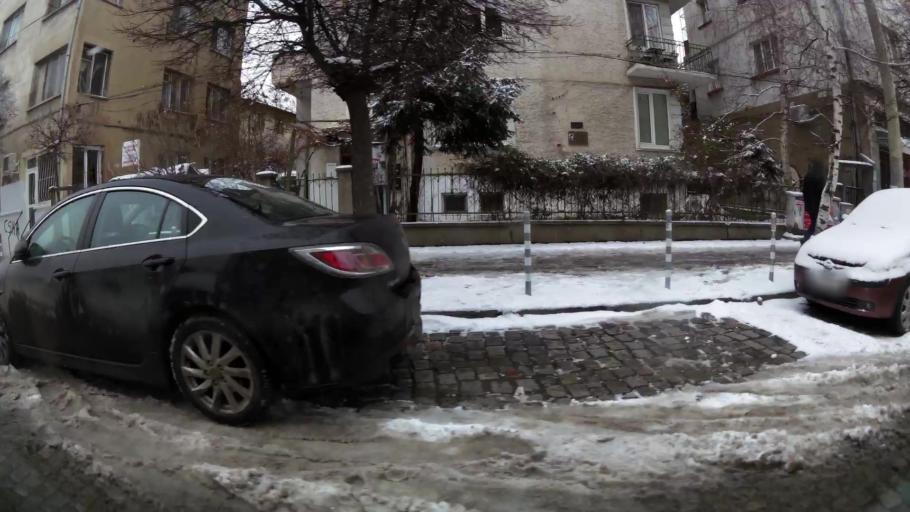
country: BG
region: Sofia-Capital
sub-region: Stolichna Obshtina
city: Sofia
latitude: 42.6878
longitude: 23.3467
